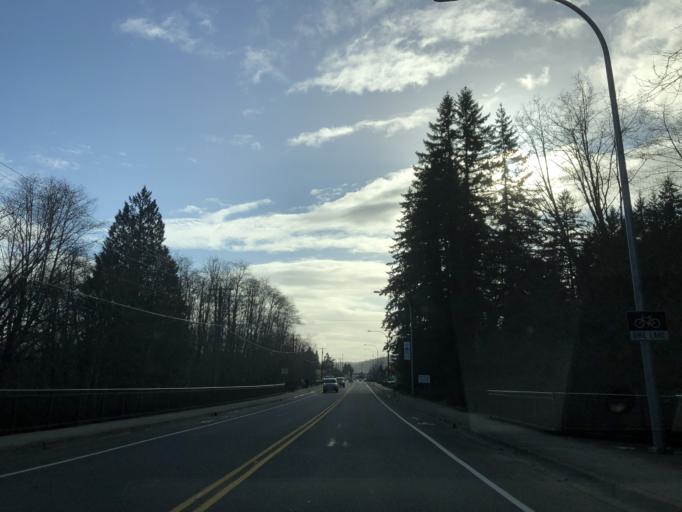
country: US
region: Washington
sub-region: Kitsap County
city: Poulsbo
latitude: 47.7519
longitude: -122.6538
